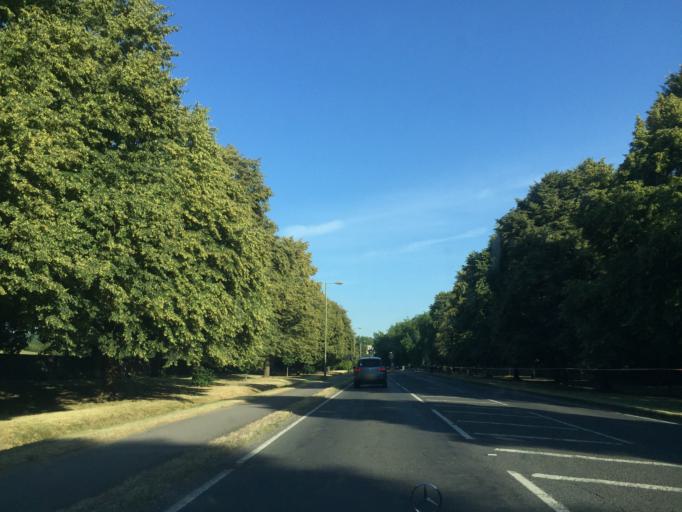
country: GB
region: England
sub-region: Oxfordshire
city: Henley on Thames
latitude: 51.5465
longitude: -0.9144
